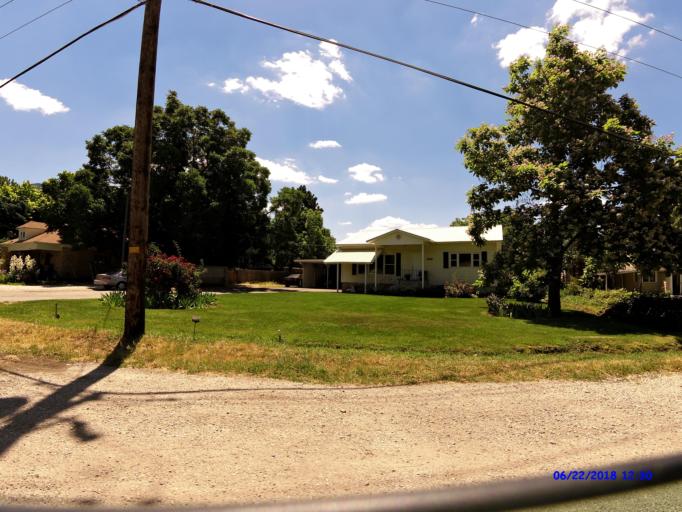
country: US
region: Utah
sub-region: Weber County
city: Ogden
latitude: 41.2412
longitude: -111.9562
